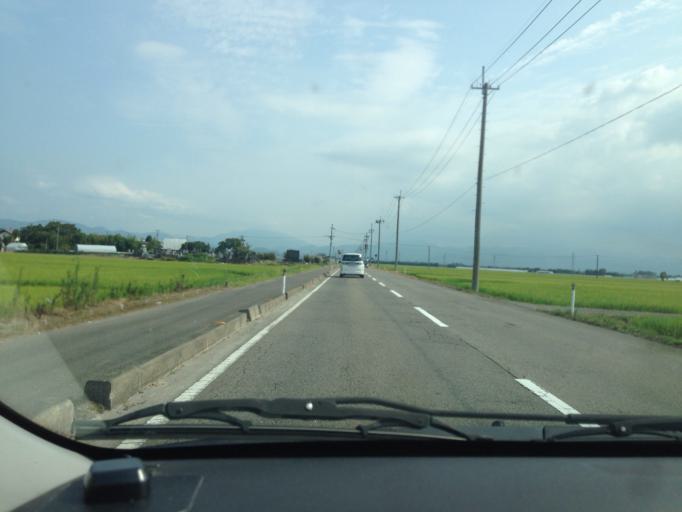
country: JP
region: Fukushima
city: Kitakata
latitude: 37.5430
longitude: 139.8570
